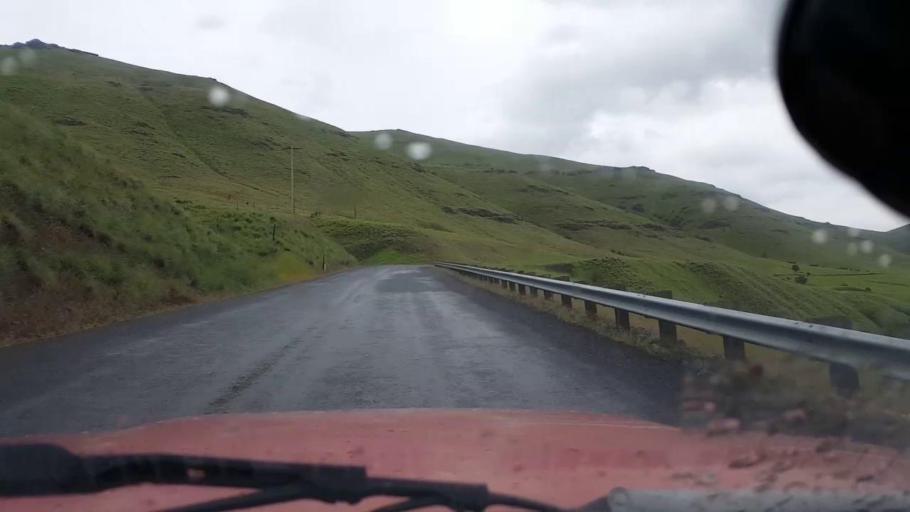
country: US
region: Washington
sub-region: Asotin County
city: Asotin
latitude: 46.0405
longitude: -117.2939
